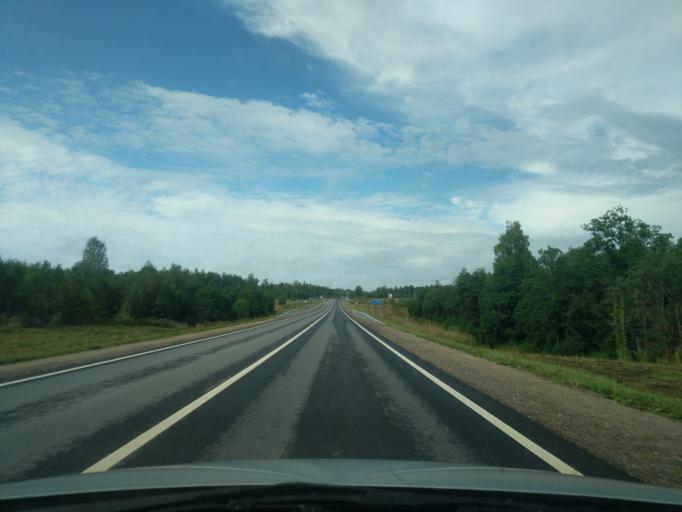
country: RU
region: Kostroma
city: Sudislavl'
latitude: 57.8280
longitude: 41.8902
